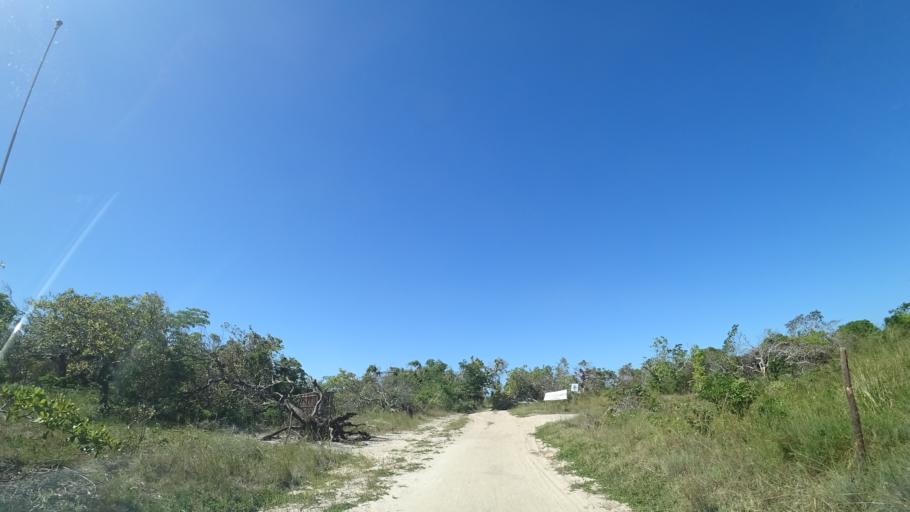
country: MZ
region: Sofala
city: Beira
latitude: -19.5739
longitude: 35.2259
